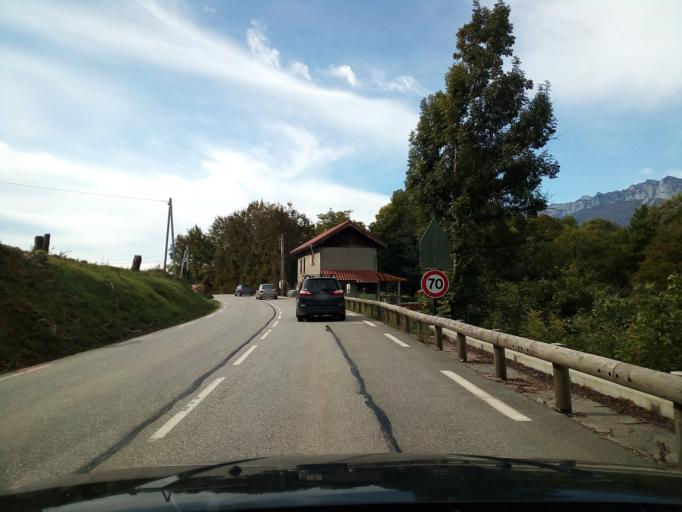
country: FR
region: Rhone-Alpes
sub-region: Departement de l'Isere
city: Le Cheylas
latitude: 45.3648
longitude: 6.0042
